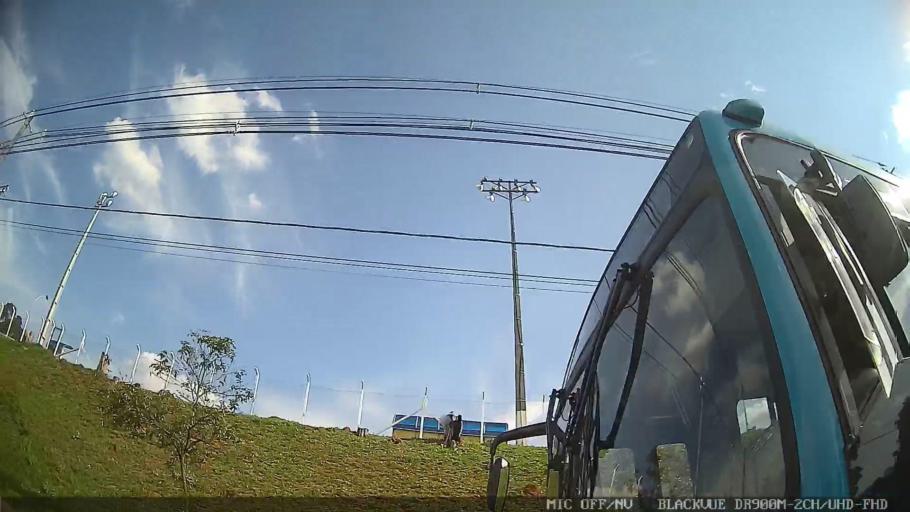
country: BR
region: Sao Paulo
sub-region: Braganca Paulista
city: Braganca Paulista
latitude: -22.9504
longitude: -46.5308
